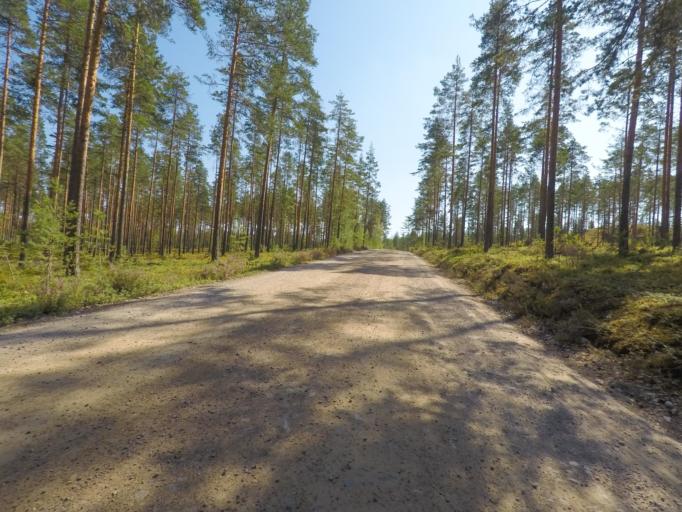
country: FI
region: Southern Savonia
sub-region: Mikkeli
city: Puumala
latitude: 61.4172
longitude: 28.0425
